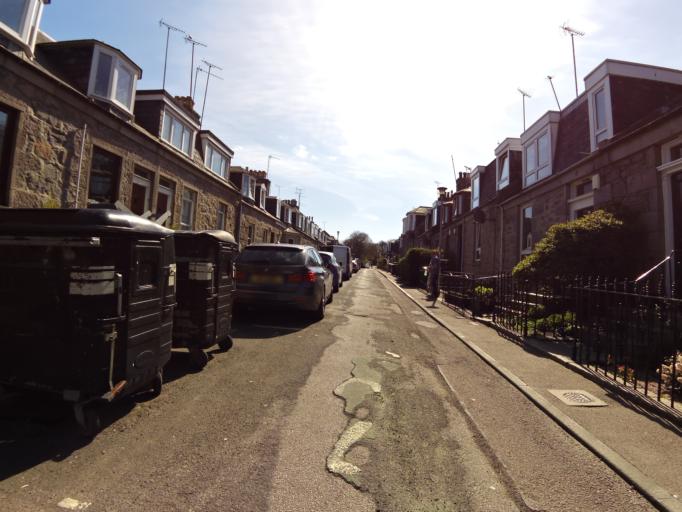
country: GB
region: Scotland
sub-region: Aberdeen City
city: Aberdeen
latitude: 57.1379
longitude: -2.0988
